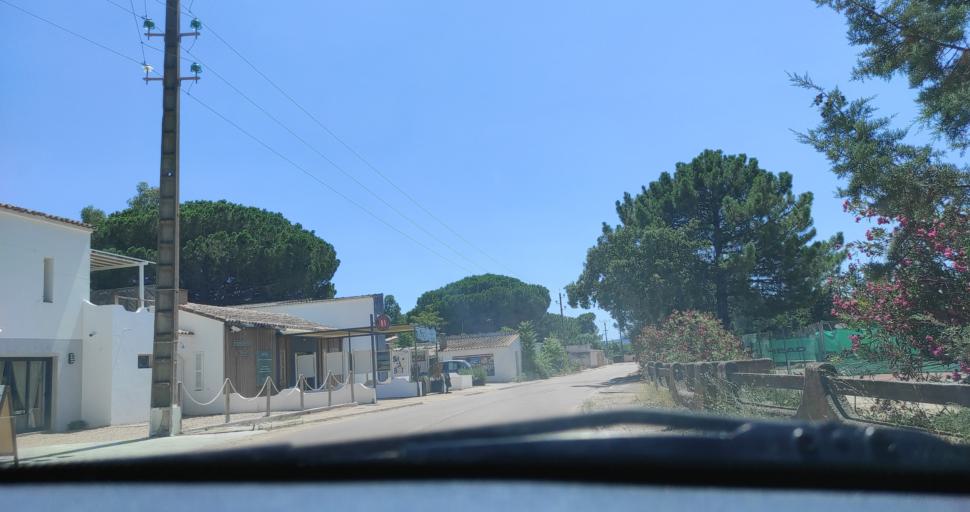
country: FR
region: Corsica
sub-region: Departement de la Corse-du-Sud
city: Porto-Vecchio
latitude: 41.6294
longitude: 9.3341
